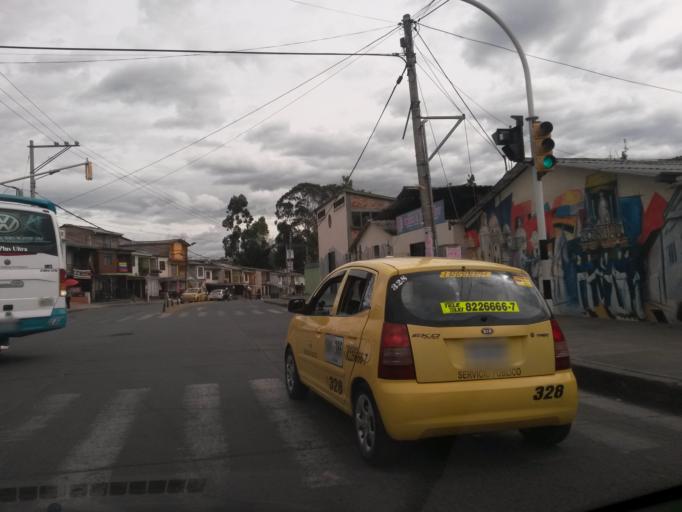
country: CO
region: Cauca
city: Popayan
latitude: 2.4453
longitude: -76.6213
